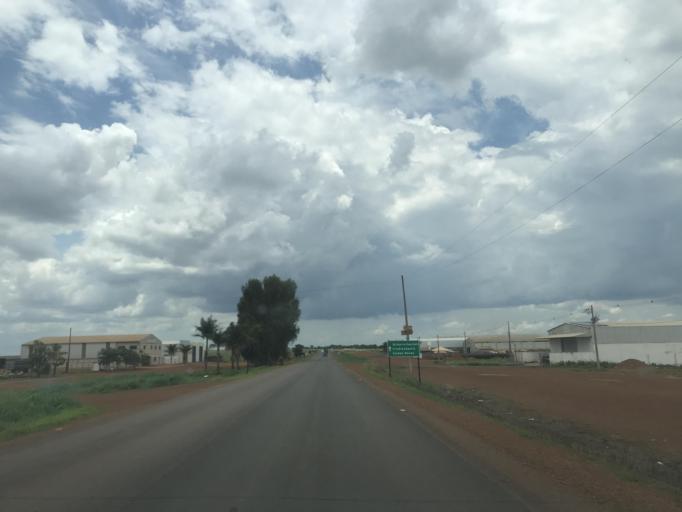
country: BR
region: Goias
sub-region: Vianopolis
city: Vianopolis
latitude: -16.7661
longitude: -48.5220
